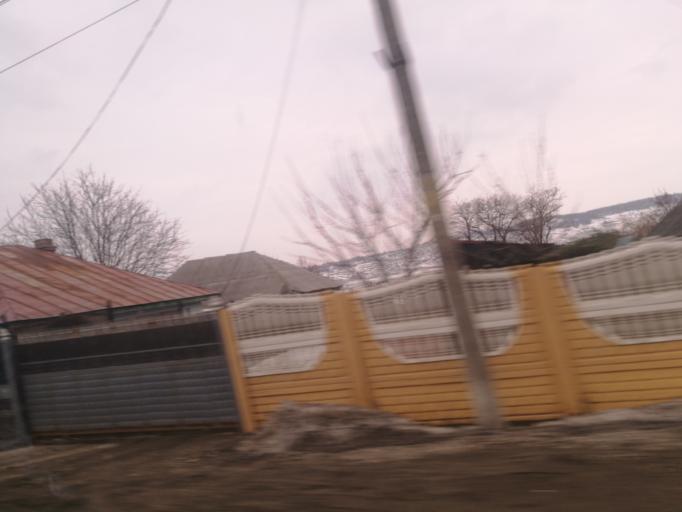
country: RO
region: Iasi
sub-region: Comuna Targu Frumos
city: Targu Frumos
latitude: 47.2039
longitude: 27.0029
